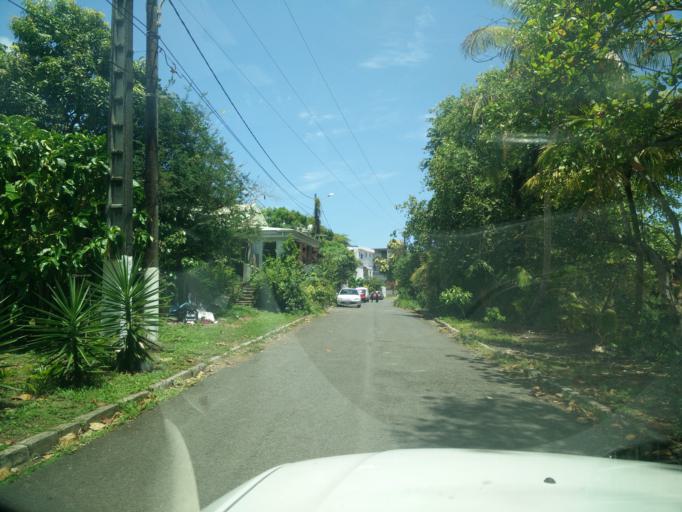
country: GP
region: Guadeloupe
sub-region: Guadeloupe
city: Trois-Rivieres
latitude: 16.0010
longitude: -61.6012
